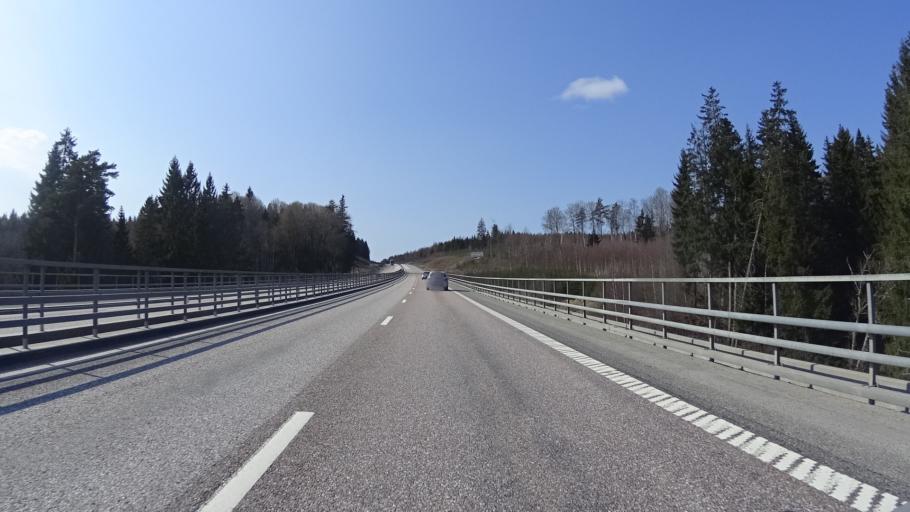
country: SE
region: OErebro
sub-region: Orebro Kommun
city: Vintrosa
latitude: 59.2542
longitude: 14.8954
